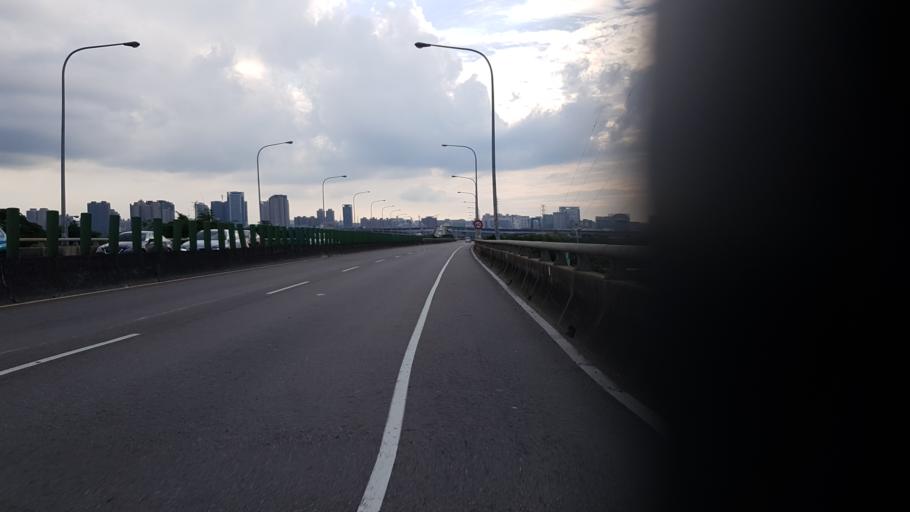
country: TW
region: Taiwan
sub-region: Hsinchu
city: Zhubei
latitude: 24.8103
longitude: 121.0213
